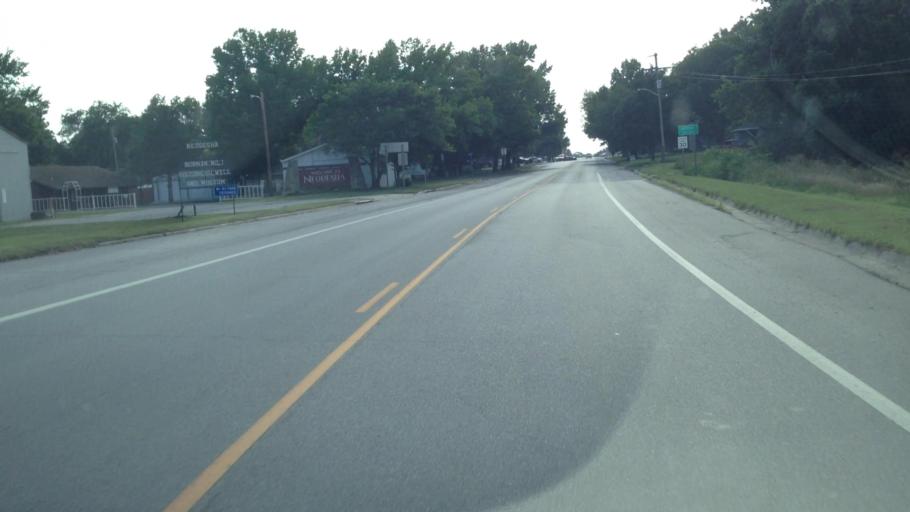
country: US
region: Kansas
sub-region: Wilson County
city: Neodesha
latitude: 37.4175
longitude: -95.6738
